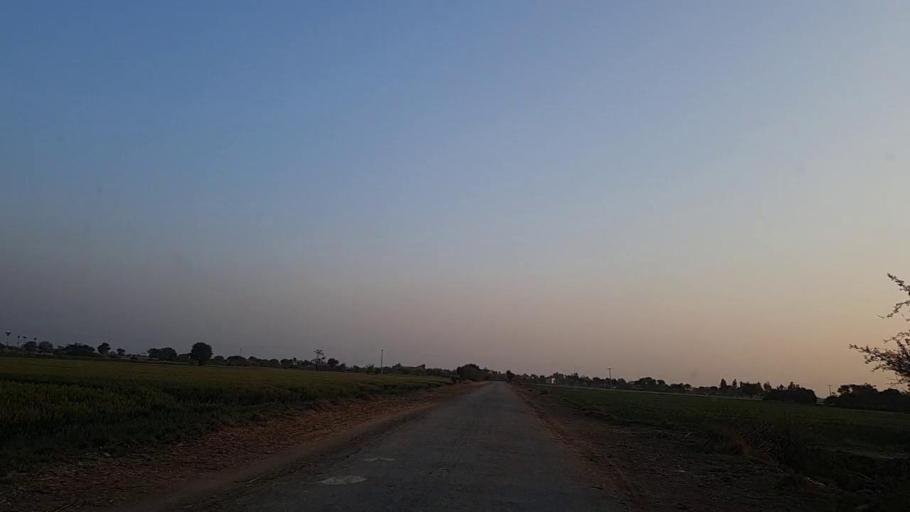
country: PK
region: Sindh
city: Shahdadpur
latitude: 25.9253
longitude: 68.5064
